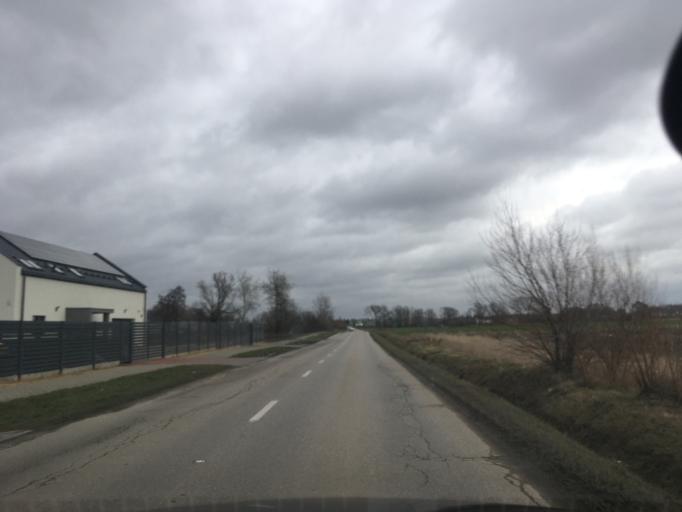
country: PL
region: Masovian Voivodeship
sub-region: Powiat pruszkowski
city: Rybie
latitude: 52.1294
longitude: 20.9654
